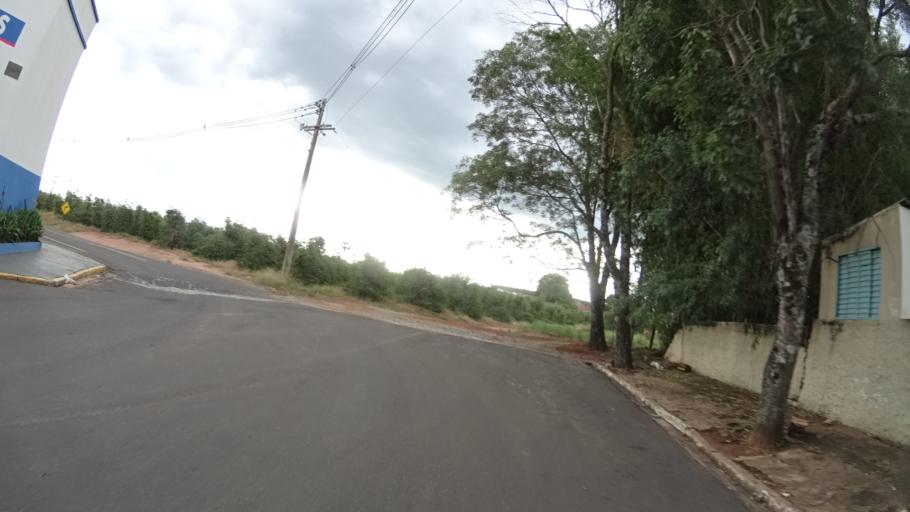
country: BR
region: Sao Paulo
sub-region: Marilia
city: Marilia
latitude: -22.2159
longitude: -49.8287
